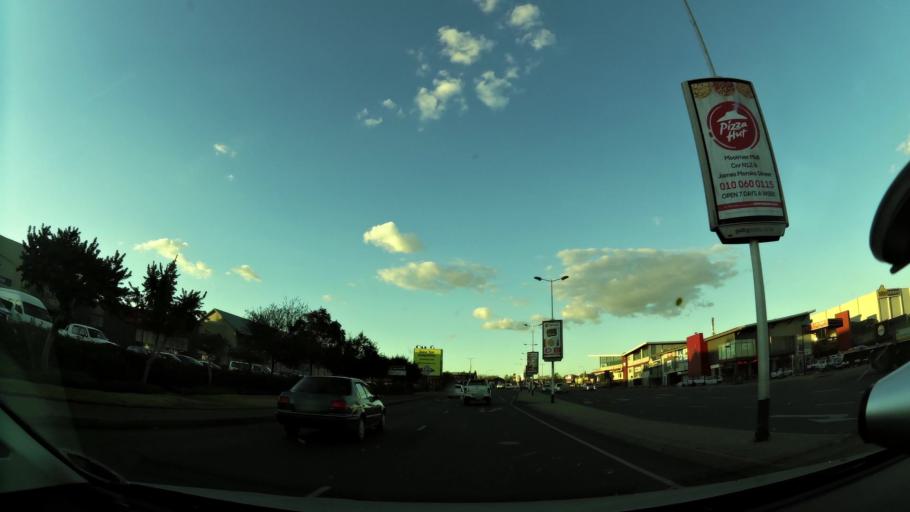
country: ZA
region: North-West
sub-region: Dr Kenneth Kaunda District Municipality
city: Potchefstroom
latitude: -26.7127
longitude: 27.1080
